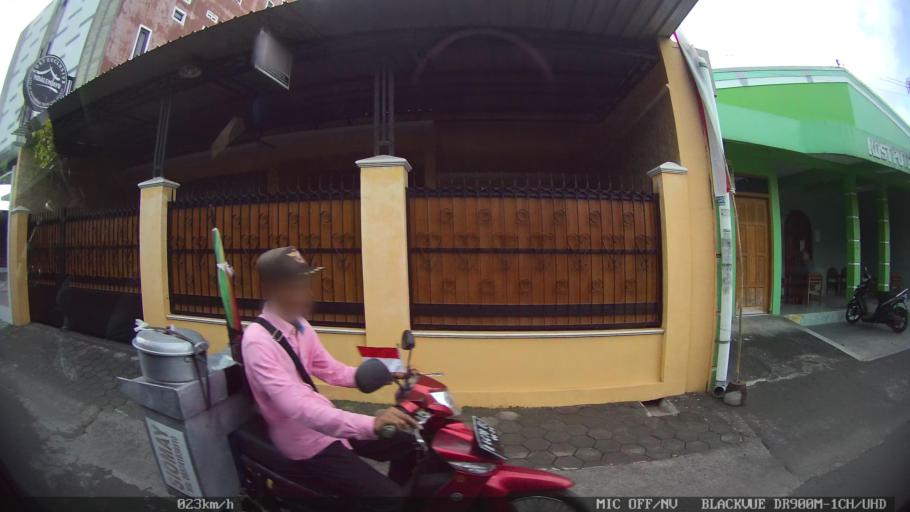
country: ID
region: Daerah Istimewa Yogyakarta
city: Gamping Lor
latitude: -7.8074
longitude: 110.3269
